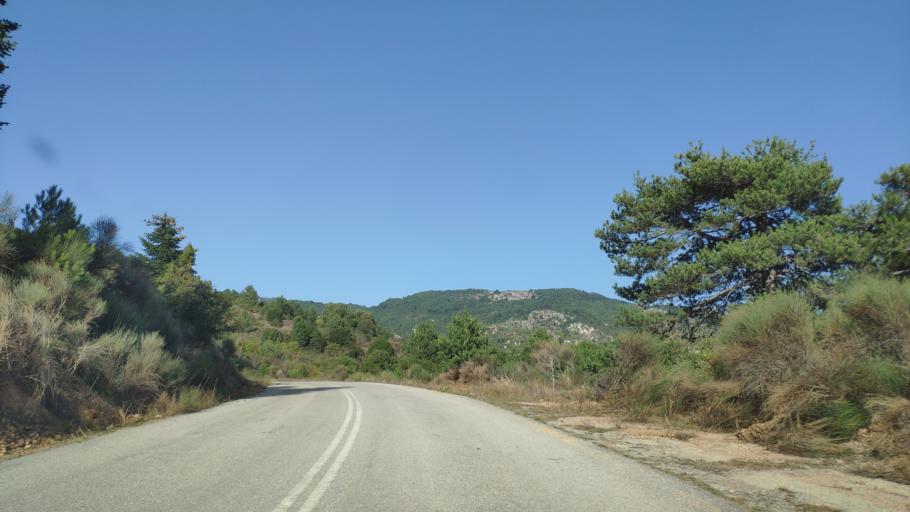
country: GR
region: West Greece
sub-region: Nomos Achaias
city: Aiyira
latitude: 38.0045
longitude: 22.3965
